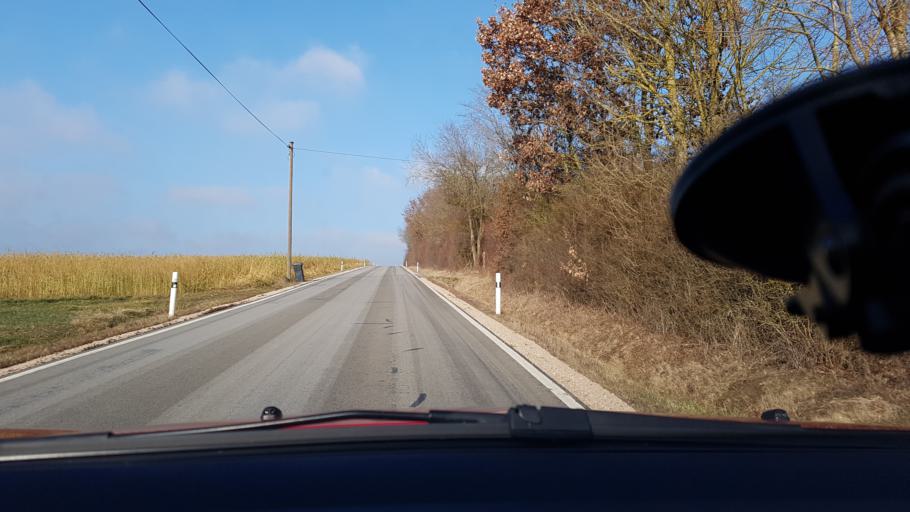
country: DE
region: Bavaria
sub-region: Lower Bavaria
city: Wittibreut
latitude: 48.3341
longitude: 12.9727
